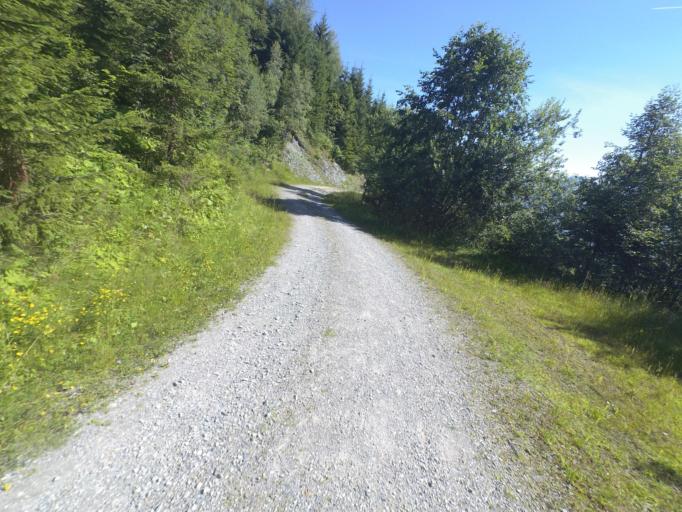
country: AT
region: Salzburg
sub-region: Politischer Bezirk Sankt Johann im Pongau
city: Sankt Veit im Pongau
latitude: 47.3530
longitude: 13.1527
